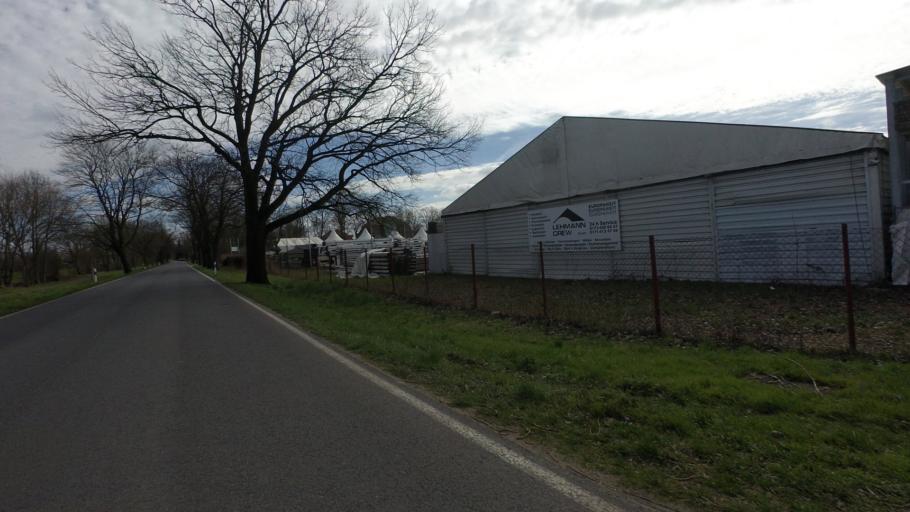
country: DE
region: Berlin
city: Blankenfelde
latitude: 52.6590
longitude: 13.4206
